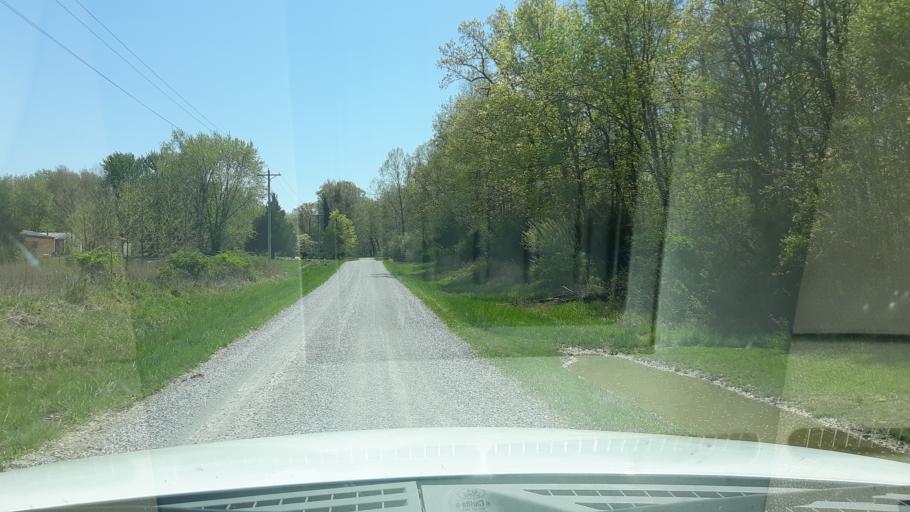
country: US
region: Illinois
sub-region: Saline County
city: Harrisburg
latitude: 37.8701
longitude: -88.6422
